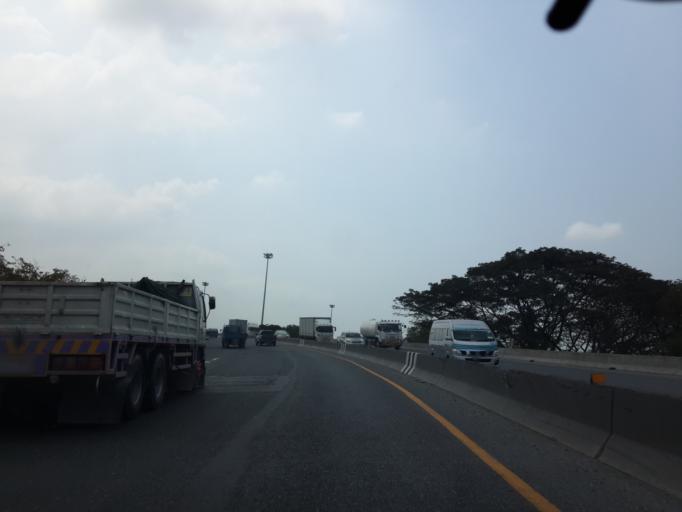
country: TH
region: Chon Buri
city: Chon Buri
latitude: 13.3348
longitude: 100.9890
